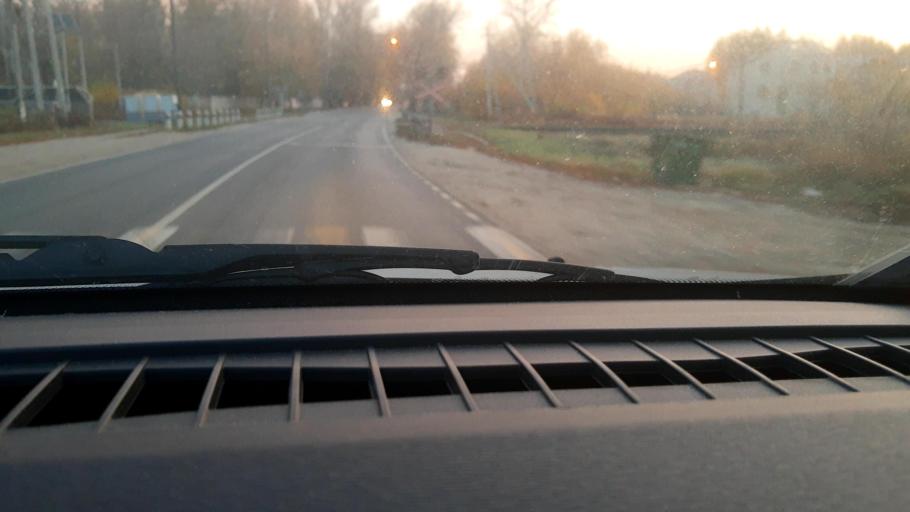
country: RU
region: Nizjnij Novgorod
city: Bor
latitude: 56.3782
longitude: 44.0316
